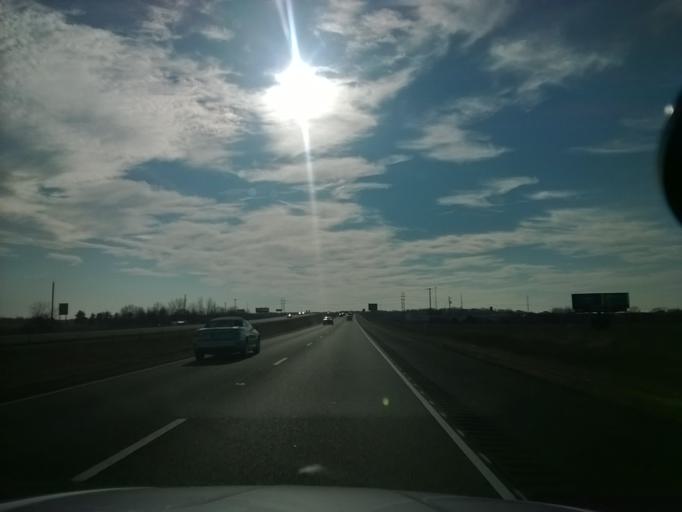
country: US
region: Indiana
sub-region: Johnson County
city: Edinburgh
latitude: 39.3160
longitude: -85.9506
